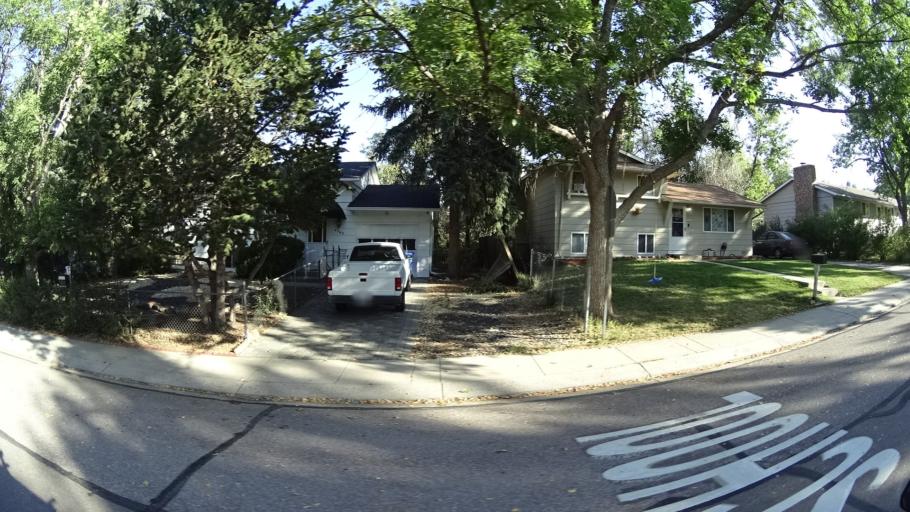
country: US
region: Colorado
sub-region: El Paso County
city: Cimarron Hills
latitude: 38.8888
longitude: -104.7402
